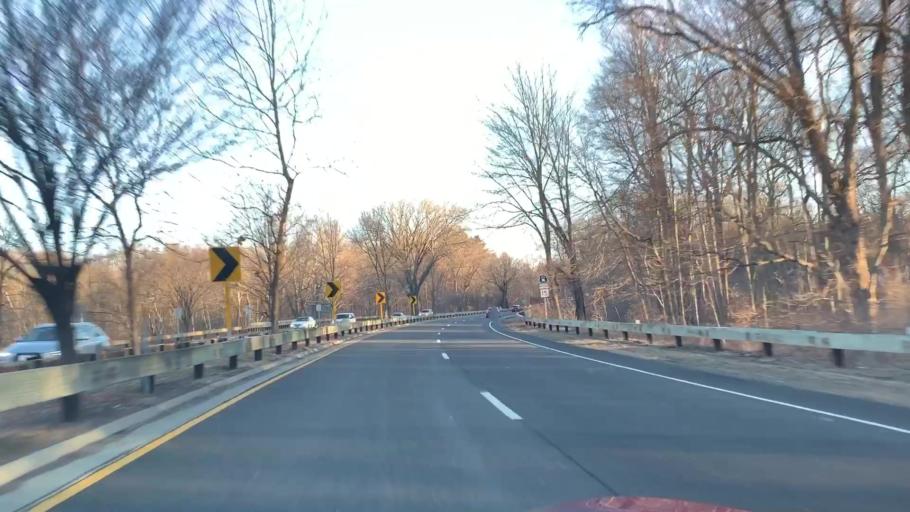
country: US
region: Connecticut
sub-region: Fairfield County
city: Glenville
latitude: 41.0850
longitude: -73.6648
